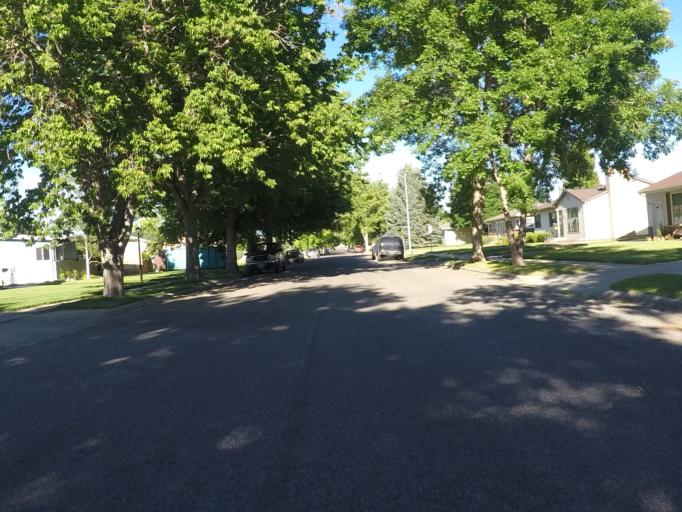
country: US
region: Montana
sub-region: Yellowstone County
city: Billings
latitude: 45.7728
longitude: -108.5852
